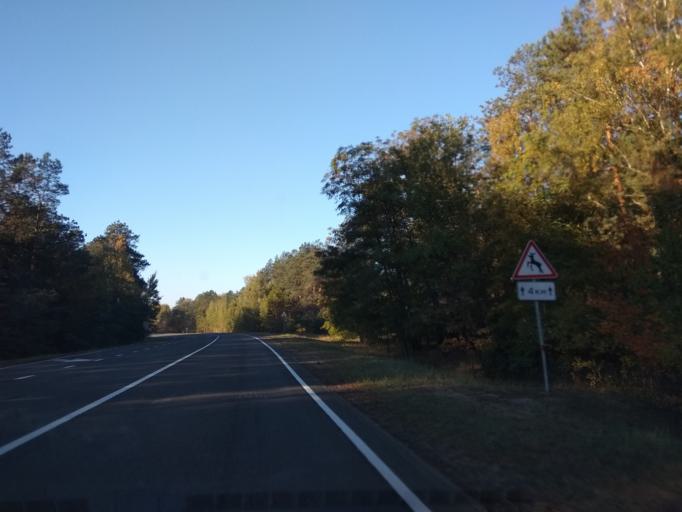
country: BY
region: Brest
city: Kobryn
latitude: 52.0095
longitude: 24.2210
